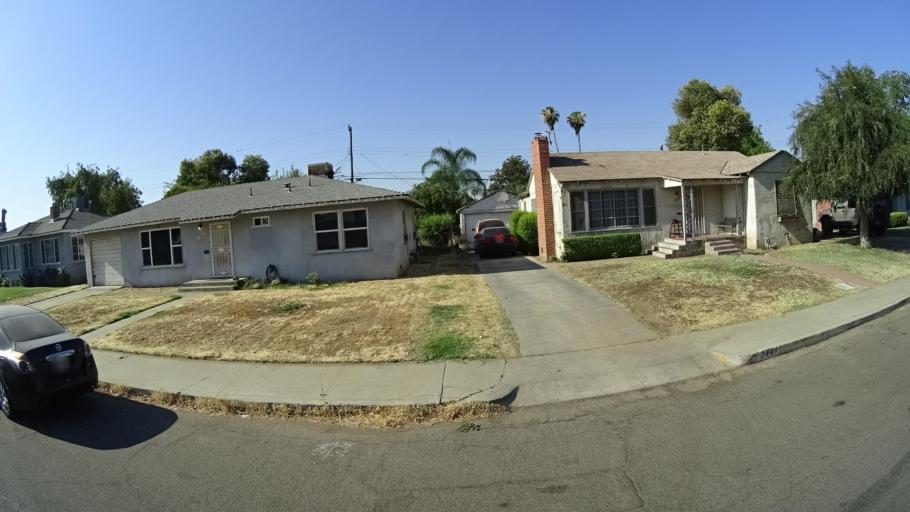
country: US
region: California
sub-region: Fresno County
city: Fresno
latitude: 36.7668
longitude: -119.7668
